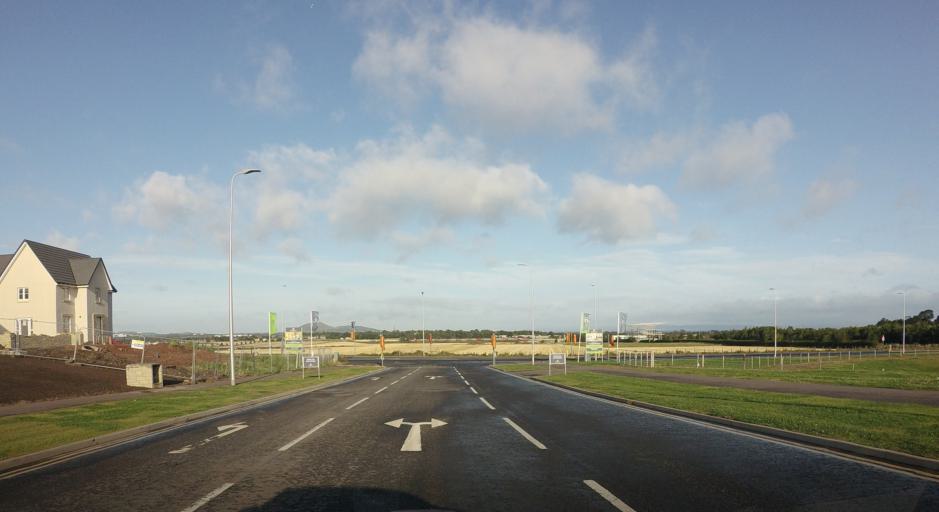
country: GB
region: Scotland
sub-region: East Lothian
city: Musselburgh
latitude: 55.9315
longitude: -3.0188
